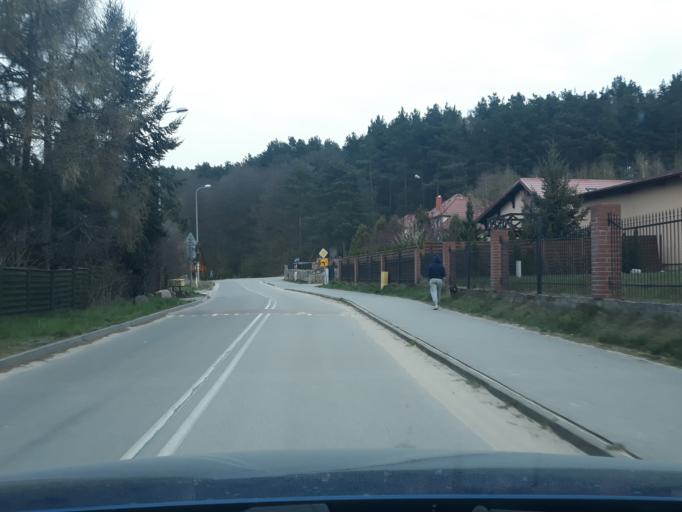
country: PL
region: Pomeranian Voivodeship
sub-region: Powiat chojnicki
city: Chojnice
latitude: 53.7281
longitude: 17.4985
